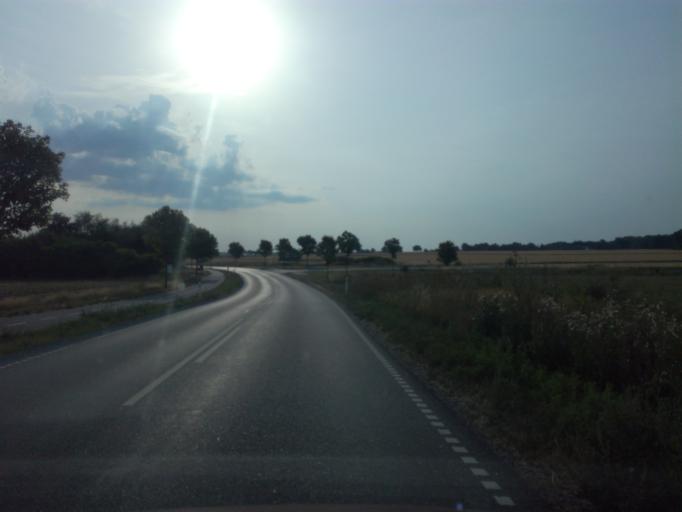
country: DK
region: South Denmark
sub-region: Vejle Kommune
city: Borkop
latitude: 55.6363
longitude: 9.6271
